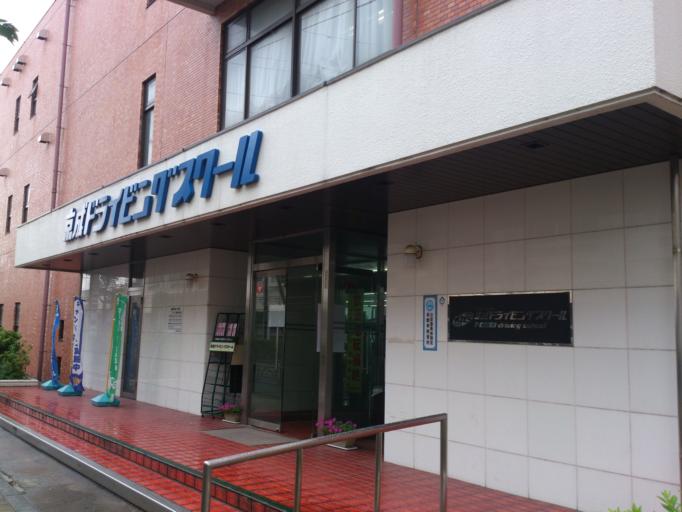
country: JP
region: Chiba
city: Matsudo
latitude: 35.7523
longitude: 139.8729
